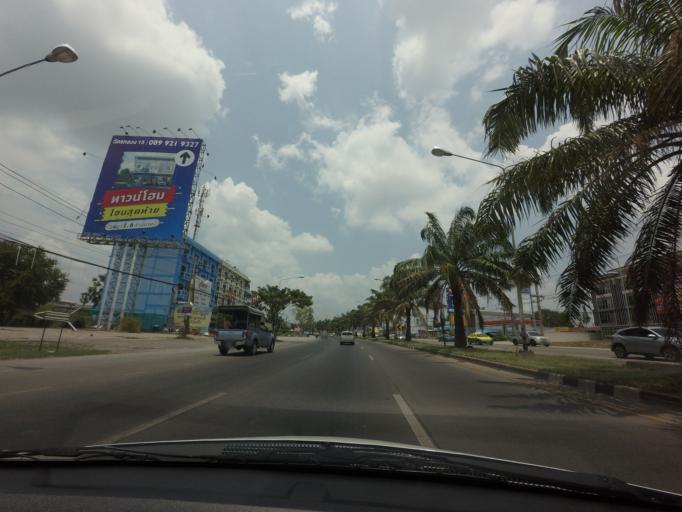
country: TH
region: Pathum Thani
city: Pathum Thani
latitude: 14.0292
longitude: 100.5351
